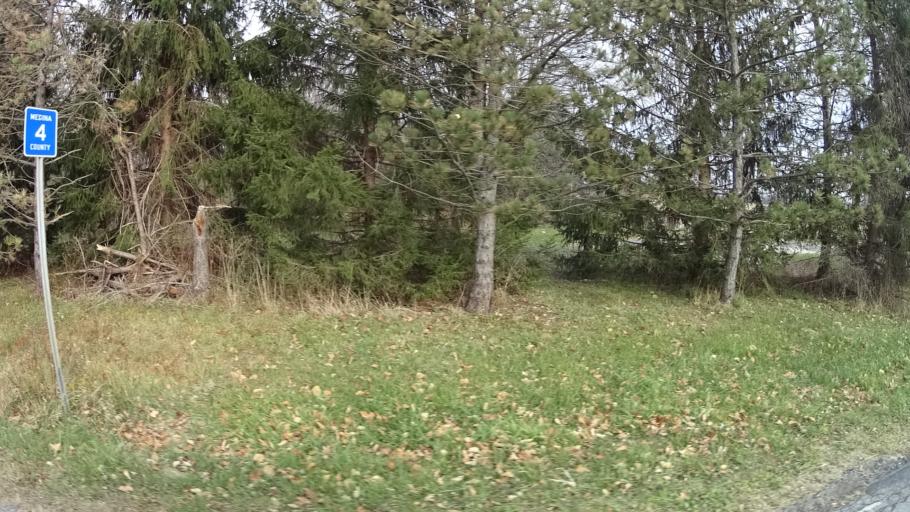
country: US
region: Ohio
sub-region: Lorain County
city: Lagrange
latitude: 41.1365
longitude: -82.0903
